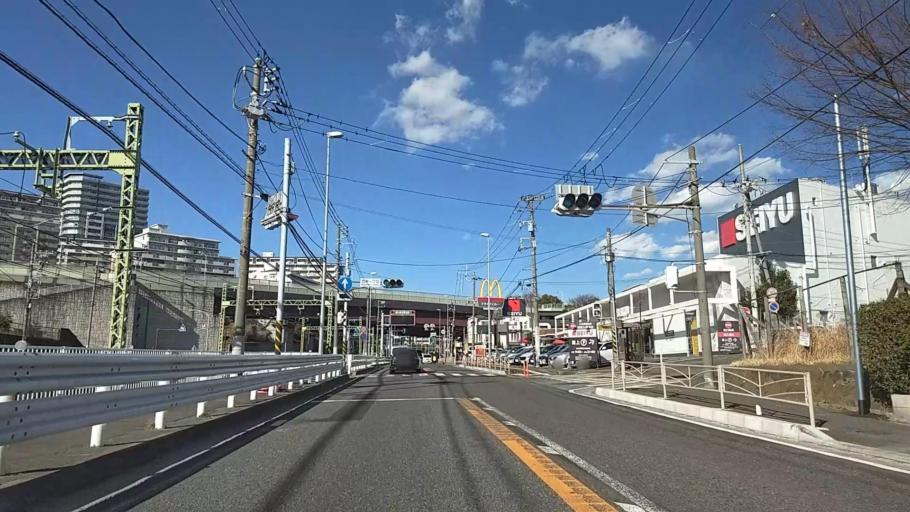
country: JP
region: Kanagawa
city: Zushi
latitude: 35.3546
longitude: 139.6282
